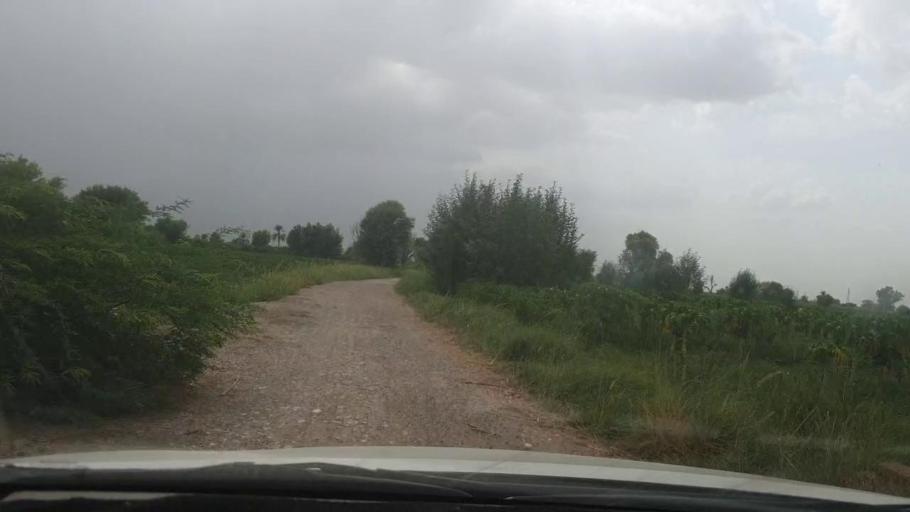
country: PK
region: Sindh
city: Kot Diji
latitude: 27.3354
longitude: 69.0051
